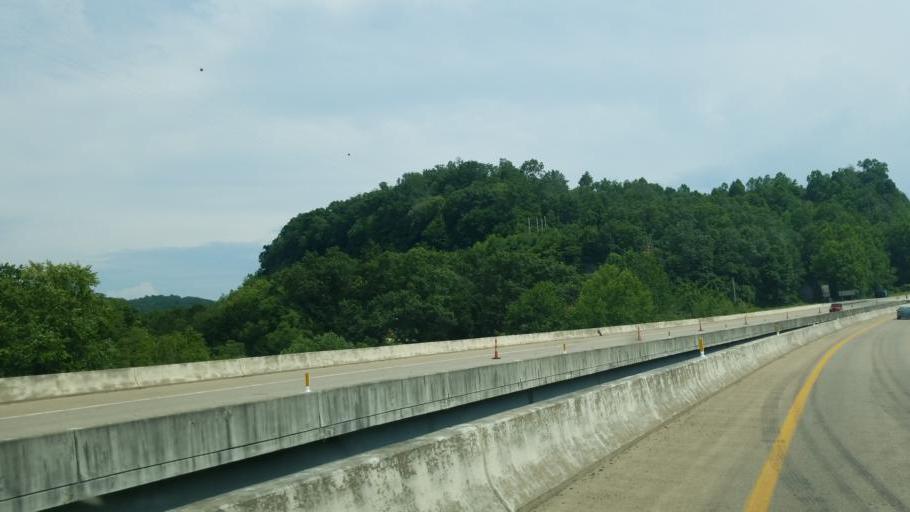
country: US
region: West Virginia
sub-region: Kanawha County
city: Alum Creek
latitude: 38.2232
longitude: -81.8352
